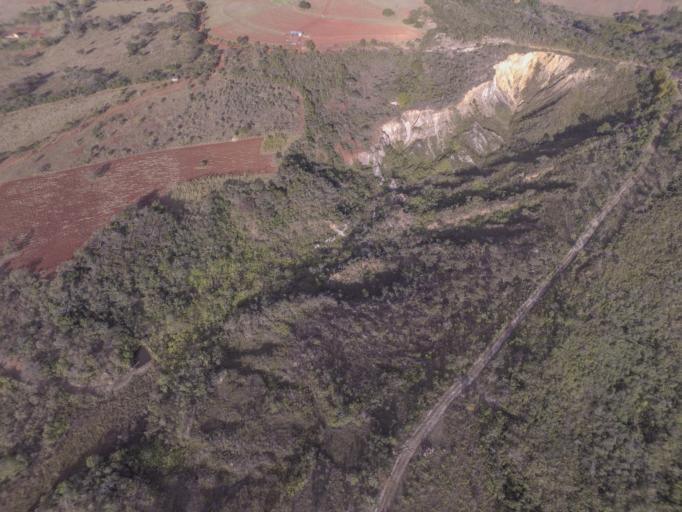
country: BR
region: Minas Gerais
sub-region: Tiradentes
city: Tiradentes
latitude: -21.0568
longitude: -44.1044
